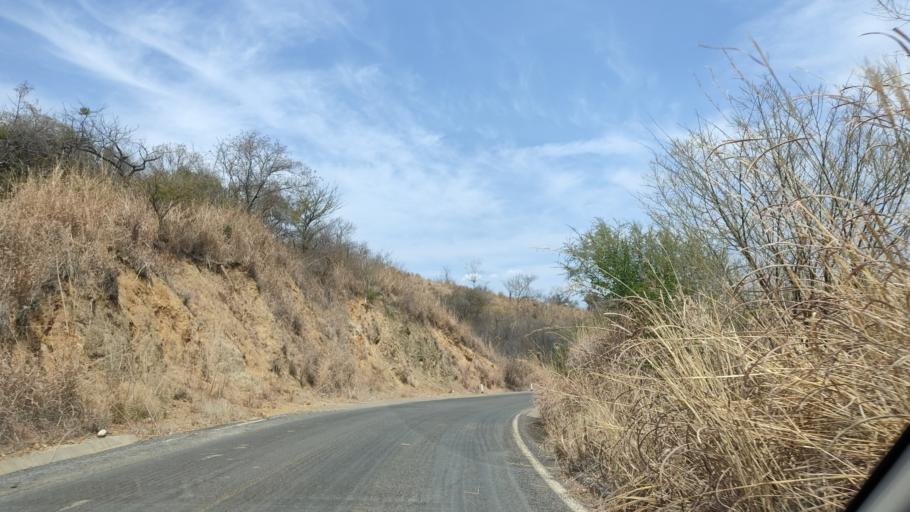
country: MX
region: Nayarit
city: Santa Maria del Oro
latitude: 21.5051
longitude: -104.6142
